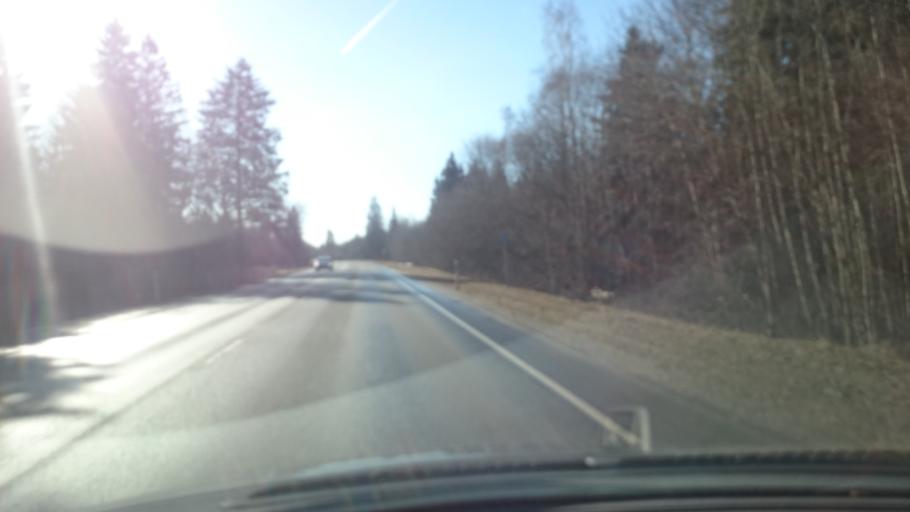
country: EE
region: Raplamaa
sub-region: Kohila vald
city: Kohila
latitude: 59.2465
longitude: 24.7481
